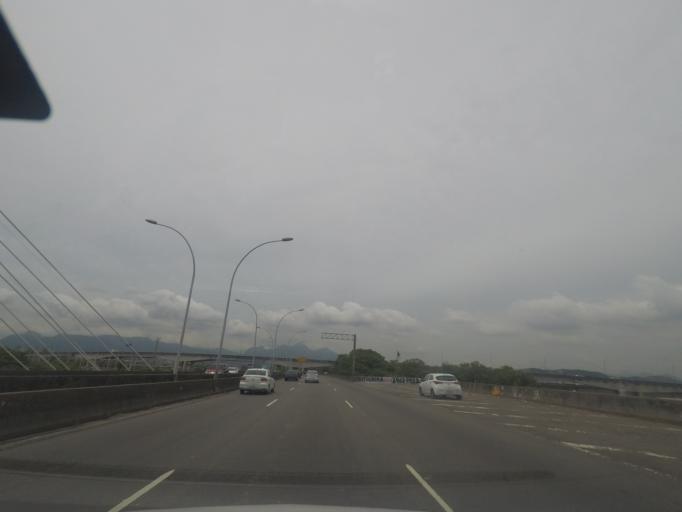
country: BR
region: Rio de Janeiro
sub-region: Rio De Janeiro
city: Rio de Janeiro
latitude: -22.8366
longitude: -43.2415
